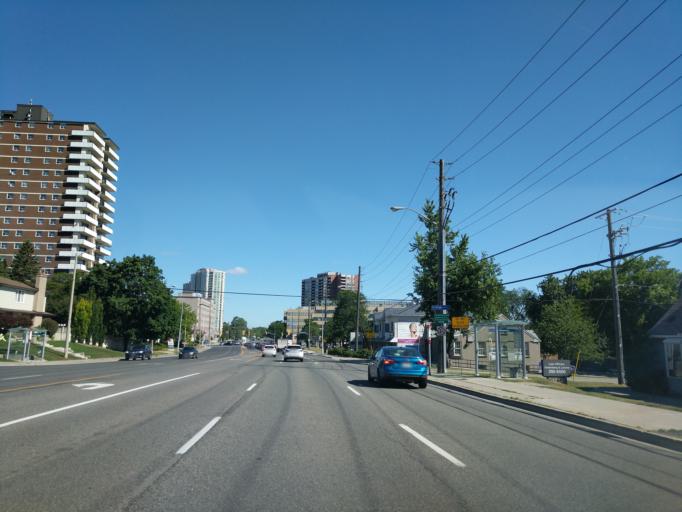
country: CA
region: Ontario
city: Scarborough
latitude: 43.7814
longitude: -79.2872
